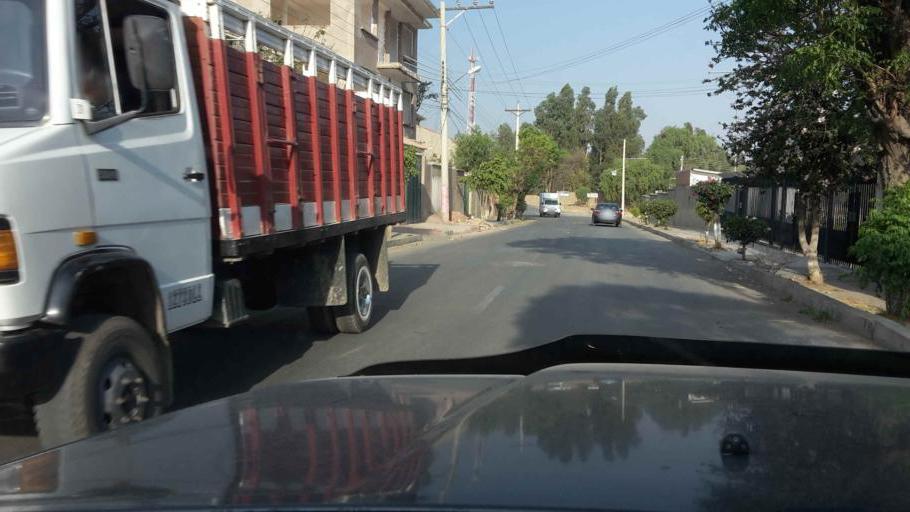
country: BO
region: Cochabamba
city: Cochabamba
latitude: -17.3411
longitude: -66.2167
